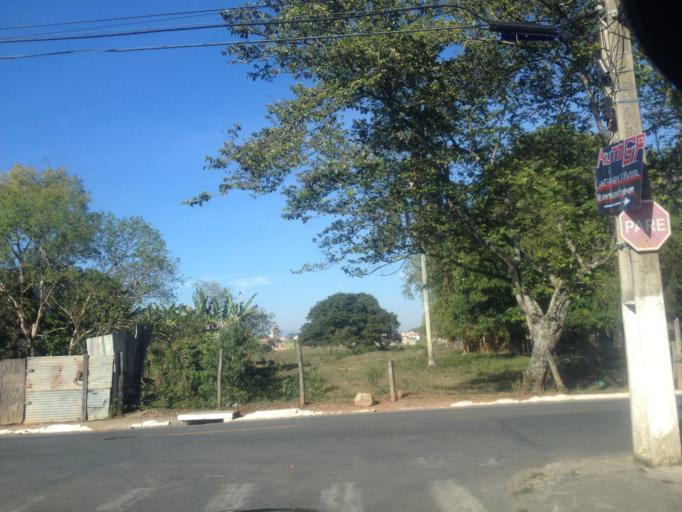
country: BR
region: Rio de Janeiro
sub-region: Porto Real
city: Porto Real
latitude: -22.4093
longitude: -44.3012
